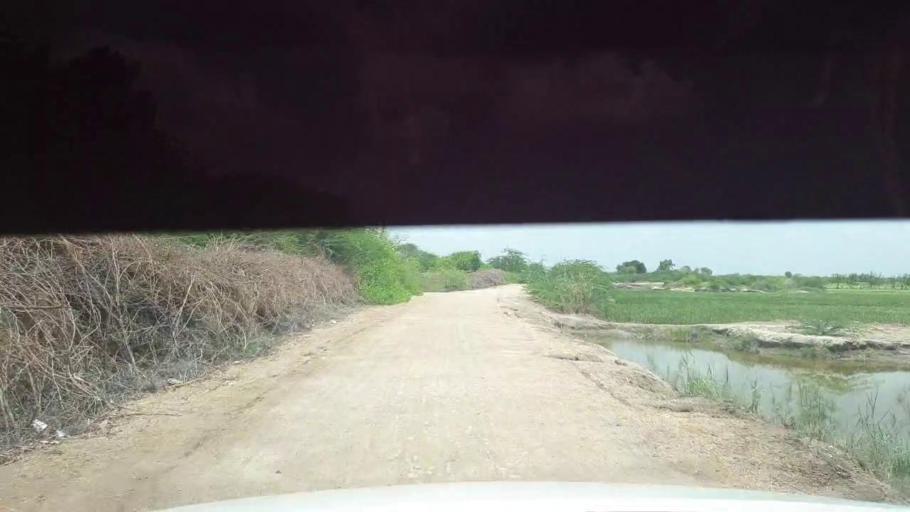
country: PK
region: Sindh
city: Kadhan
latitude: 24.4844
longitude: 69.0028
